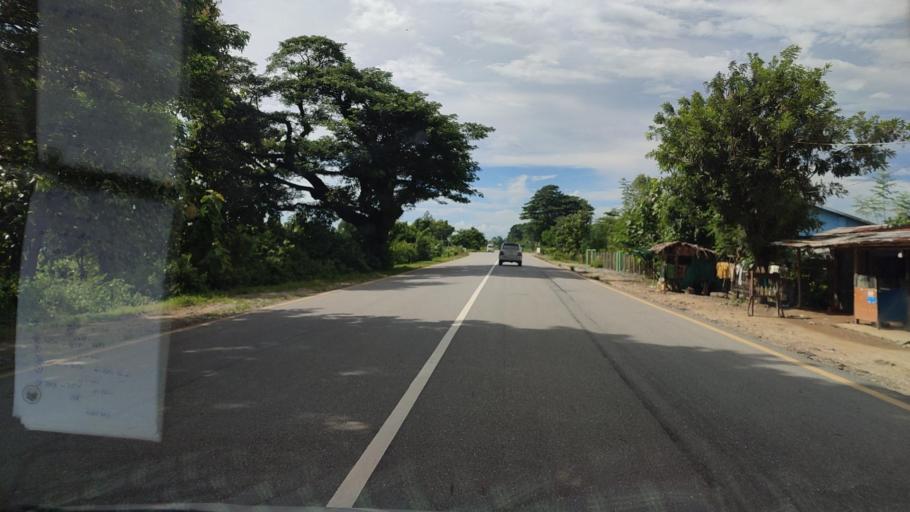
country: MM
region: Bago
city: Pyu
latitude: 18.4222
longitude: 96.4528
